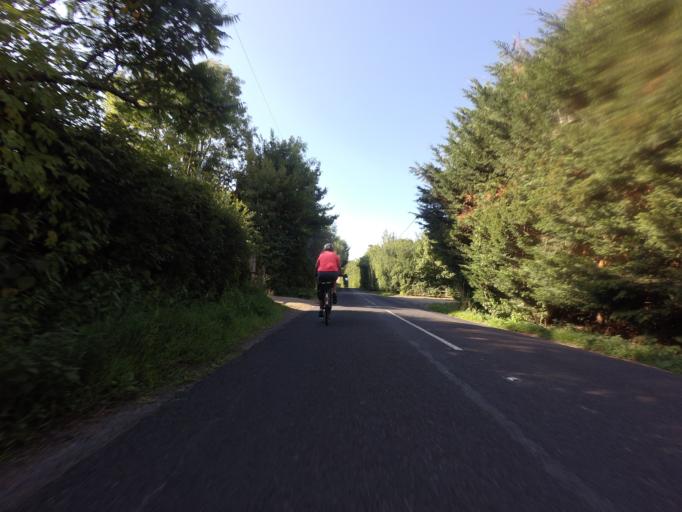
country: GB
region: England
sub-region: Kent
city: Tenterden
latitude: 51.0434
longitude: 0.6998
